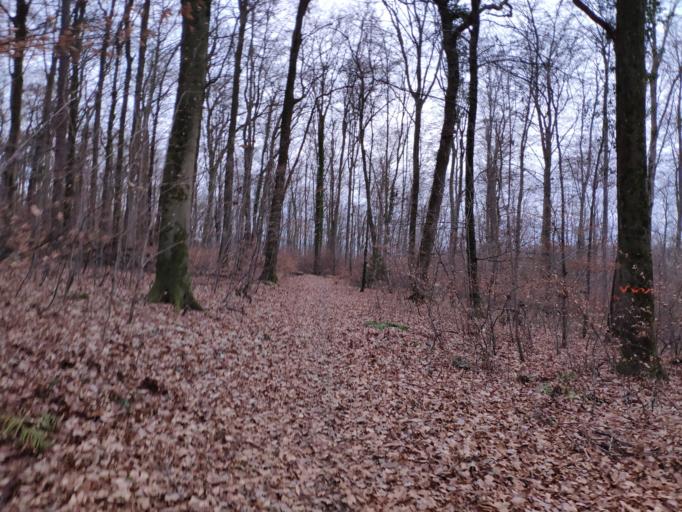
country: DE
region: Baden-Wuerttemberg
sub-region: Freiburg Region
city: Inzlingen
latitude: 47.5987
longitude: 7.6839
